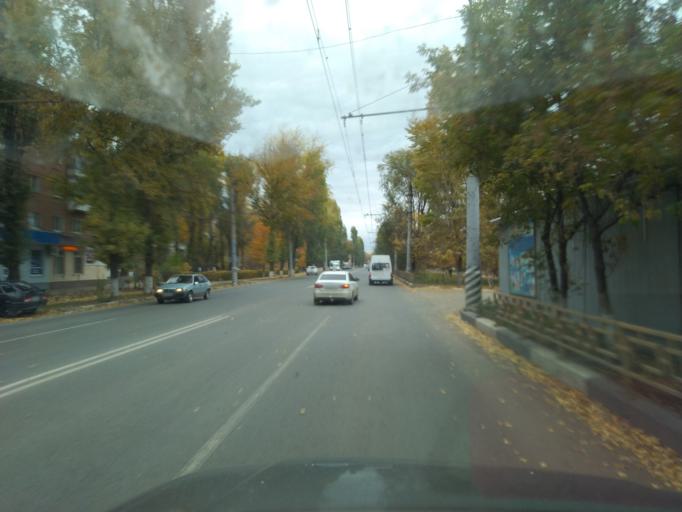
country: RU
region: Saratov
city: Engel's
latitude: 51.4753
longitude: 46.1311
